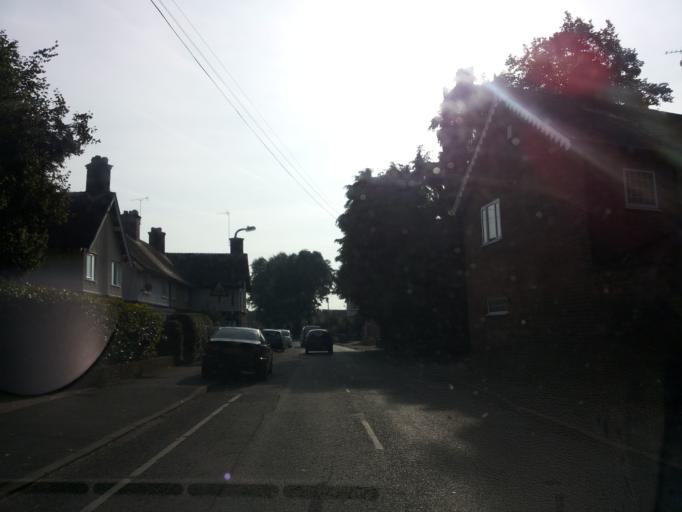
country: GB
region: England
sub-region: Worcestershire
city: Stourport-on-Severn
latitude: 52.3419
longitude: -2.2825
